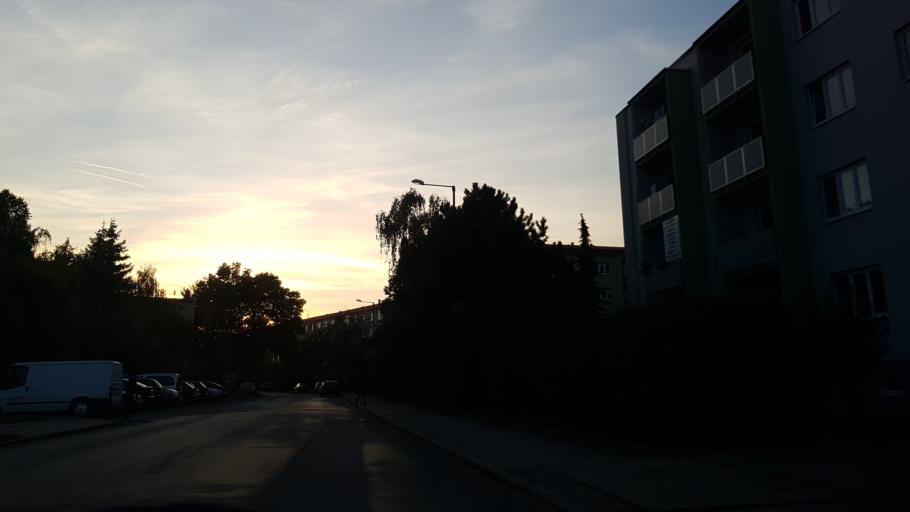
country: CZ
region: Zlin
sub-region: Okres Uherske Hradiste
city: Uherske Hradiste
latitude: 49.0604
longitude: 17.4664
